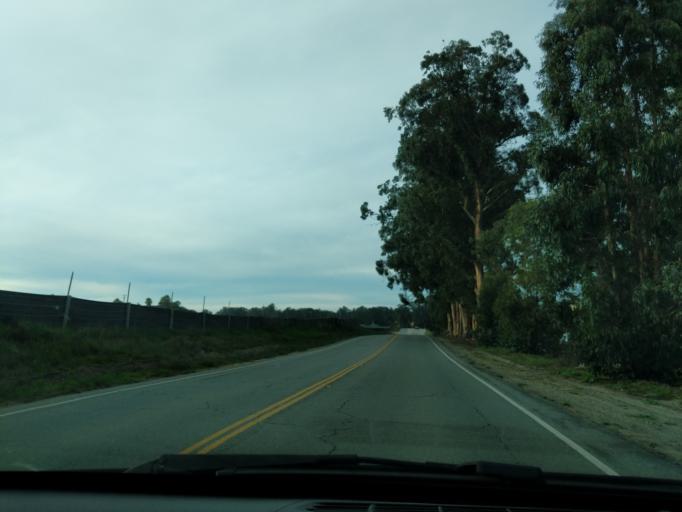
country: US
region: California
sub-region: San Luis Obispo County
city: Callender
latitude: 35.0365
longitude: -120.5638
